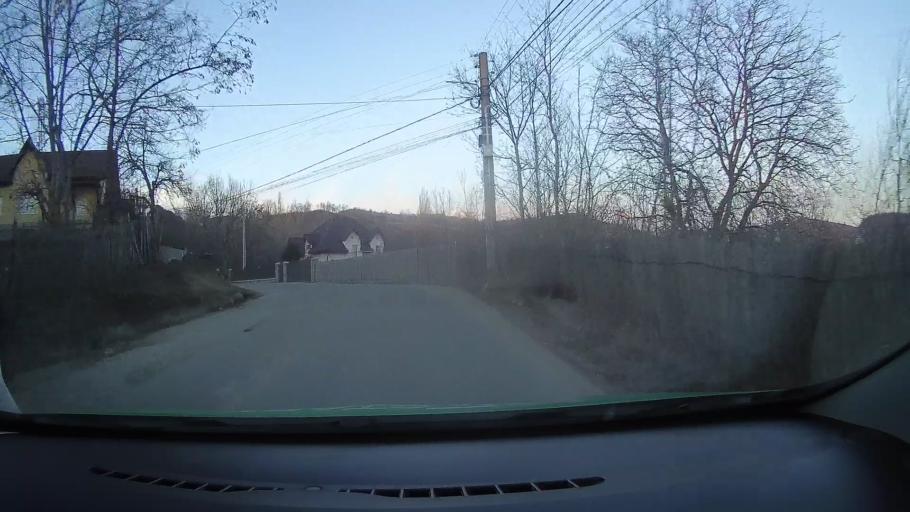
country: RO
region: Prahova
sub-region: Comuna Comarnic
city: Comarnic
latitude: 45.2559
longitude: 25.6438
